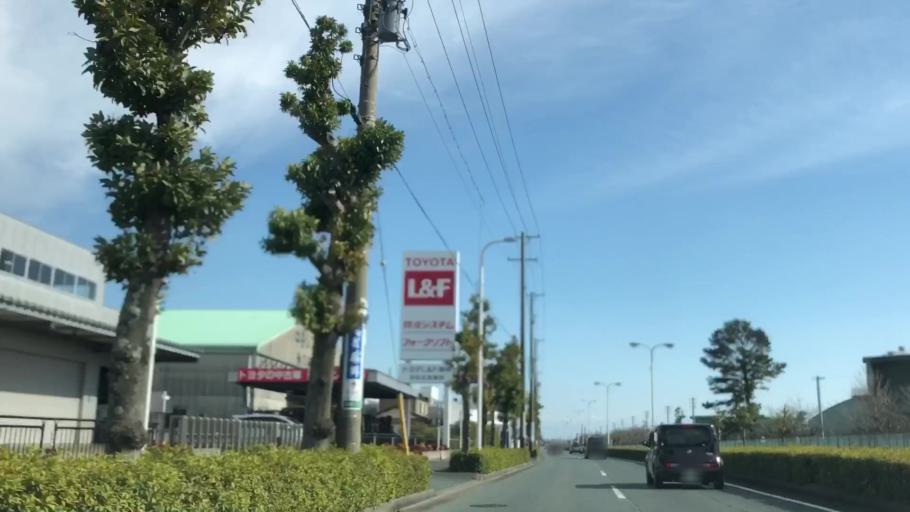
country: JP
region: Shizuoka
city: Hamamatsu
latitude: 34.7564
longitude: 137.6953
